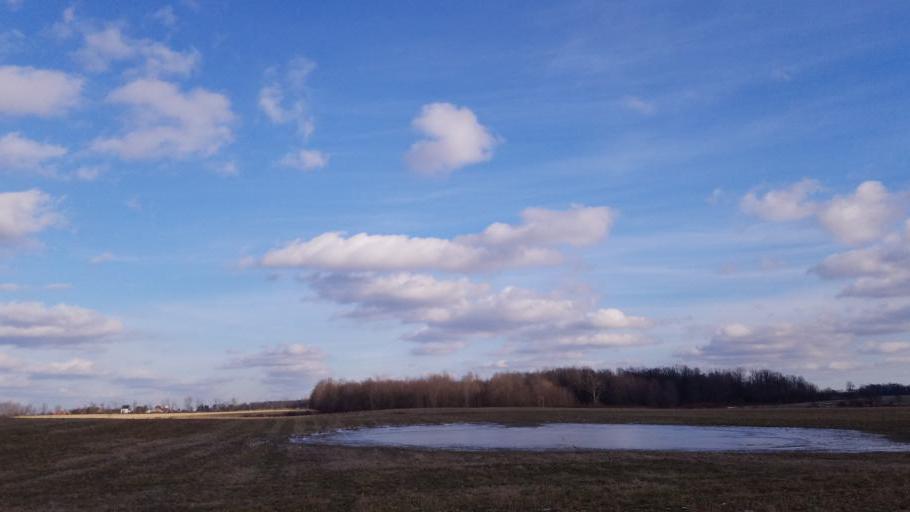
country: US
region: Ohio
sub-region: Morrow County
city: Mount Gilead
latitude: 40.6217
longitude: -82.7283
